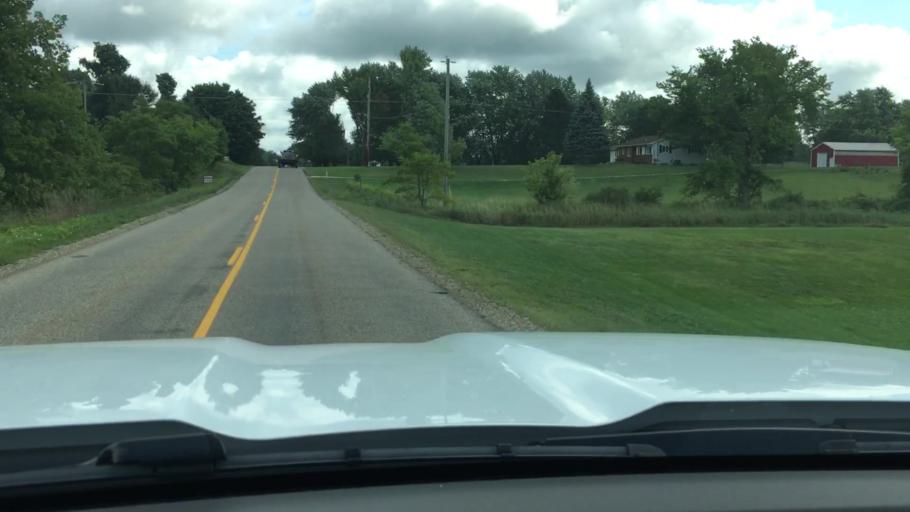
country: US
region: Michigan
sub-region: Eaton County
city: Dimondale
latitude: 42.5820
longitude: -84.6177
